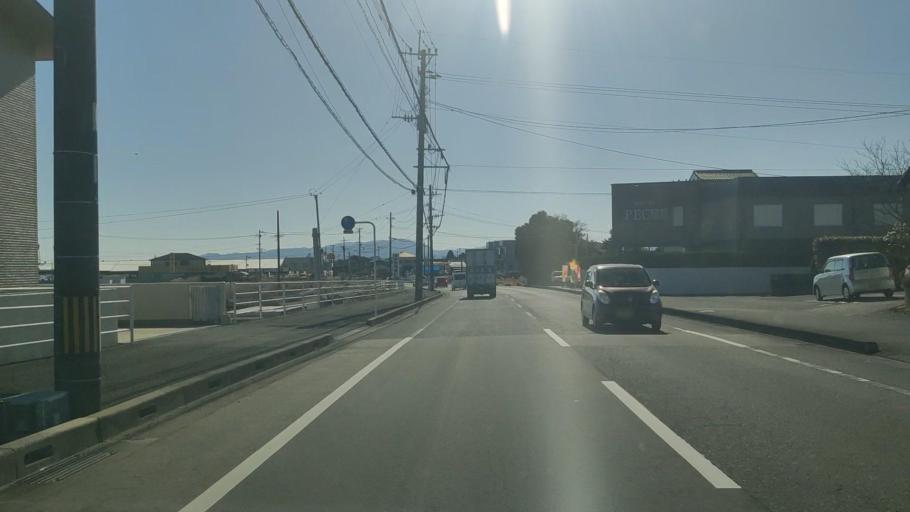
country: JP
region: Miyazaki
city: Miyazaki-shi
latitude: 31.9430
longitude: 131.4577
